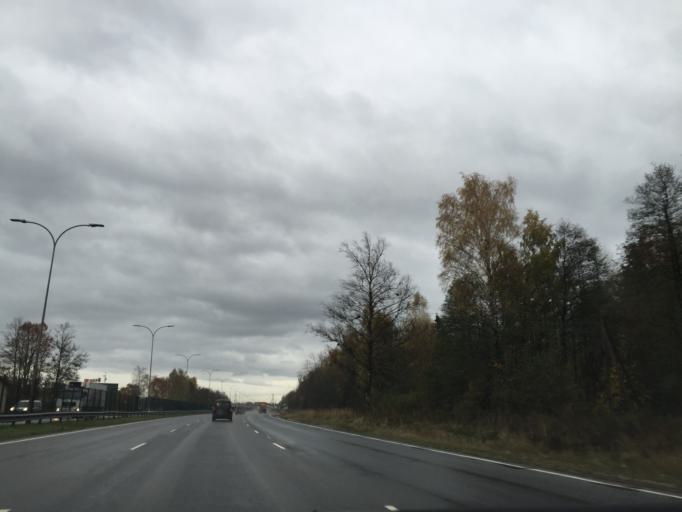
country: LV
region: Marupe
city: Marupe
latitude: 56.9457
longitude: 23.9939
